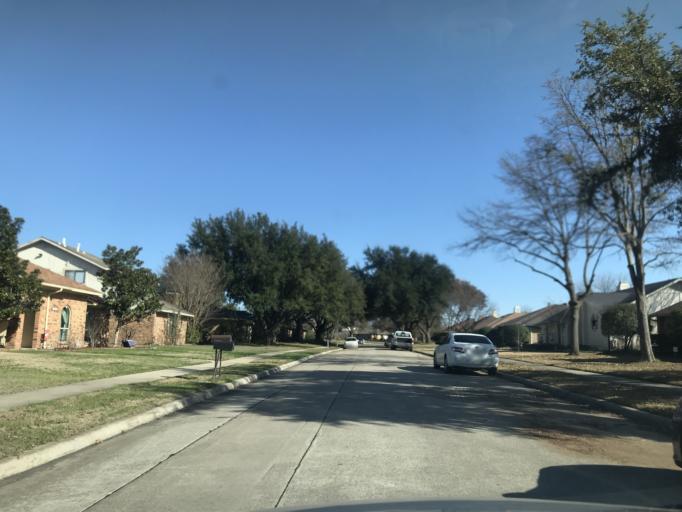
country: US
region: Texas
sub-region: Dallas County
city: Carrollton
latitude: 32.9882
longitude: -96.8711
